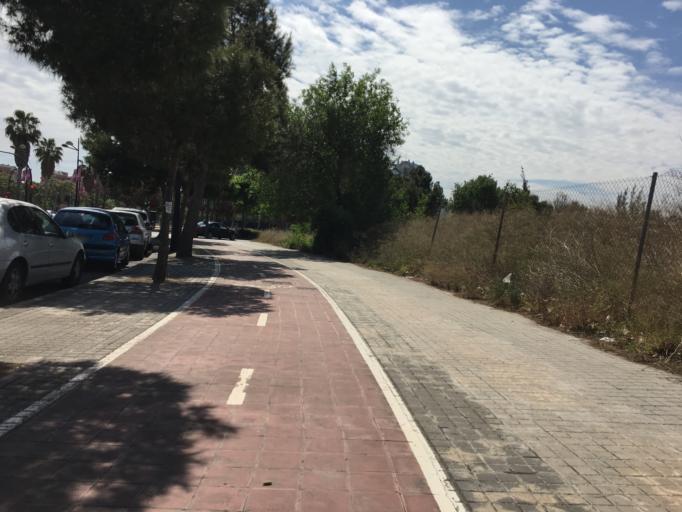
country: ES
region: Valencia
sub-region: Provincia de Valencia
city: Mislata
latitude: 39.4805
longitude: -0.4079
